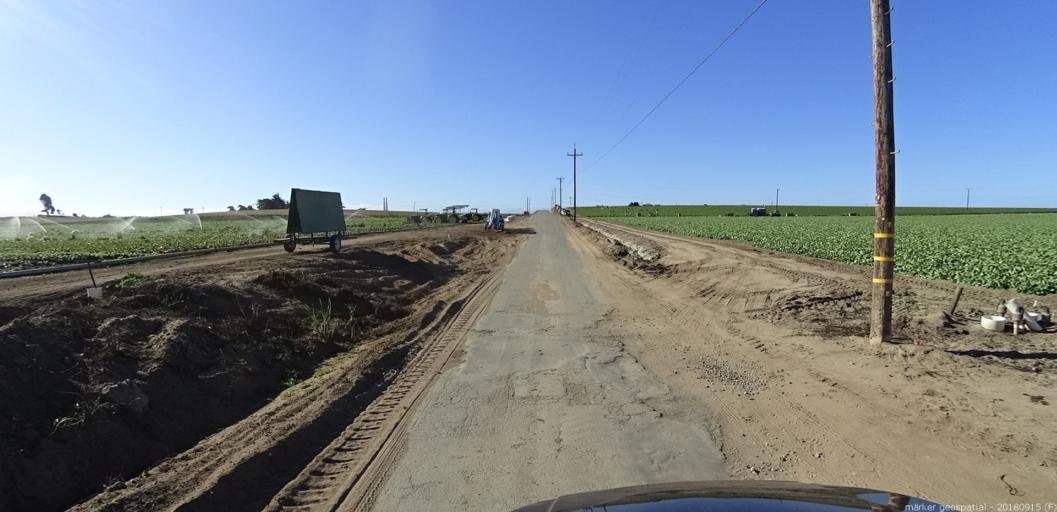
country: US
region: California
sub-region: Monterey County
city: Elkhorn
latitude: 36.8341
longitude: -121.7936
